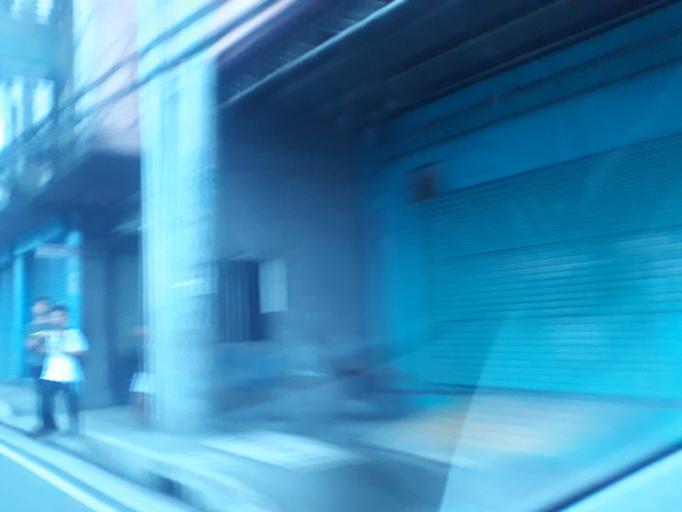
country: PH
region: Calabarzon
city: Del Monte
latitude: 14.6271
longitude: 121.0120
